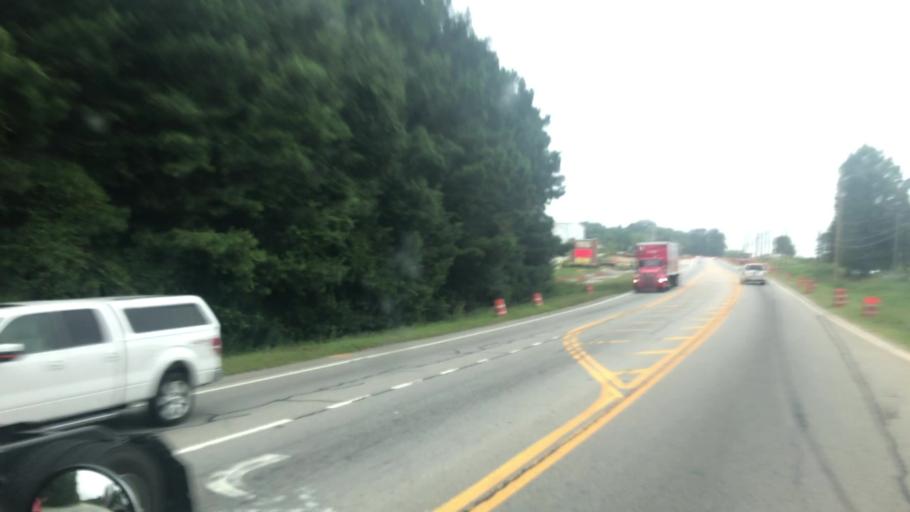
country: US
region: Georgia
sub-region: Henry County
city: McDonough
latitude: 33.3904
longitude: -84.1736
